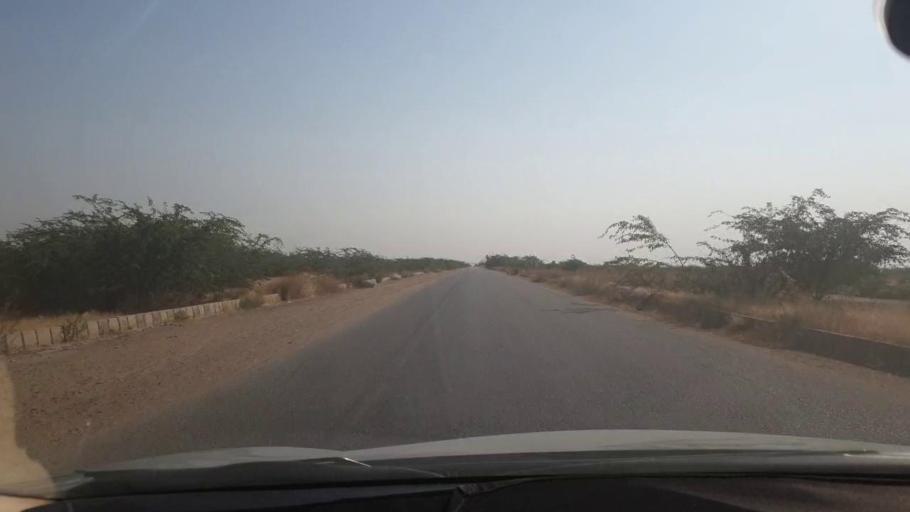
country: PK
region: Sindh
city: Malir Cantonment
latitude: 25.0714
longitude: 67.1386
